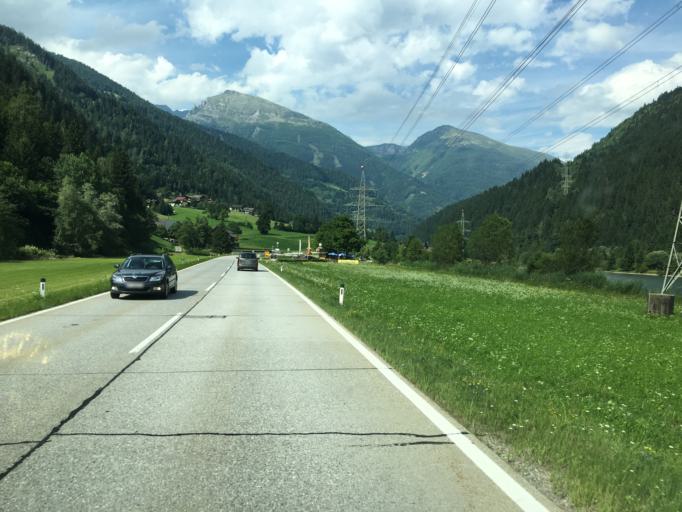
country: AT
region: Carinthia
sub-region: Politischer Bezirk Spittal an der Drau
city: Stall
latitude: 46.9128
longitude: 13.0692
